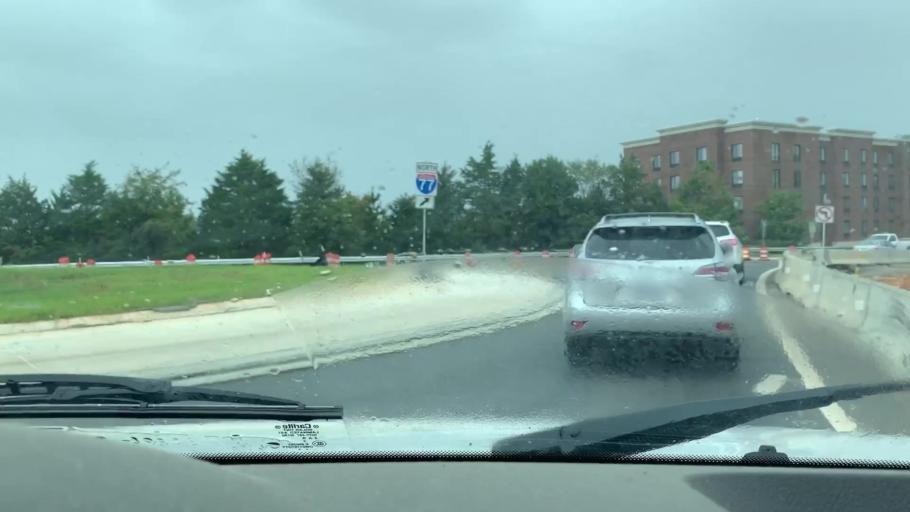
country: US
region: North Carolina
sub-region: Mecklenburg County
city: Cornelius
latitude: 35.5033
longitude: -80.8656
